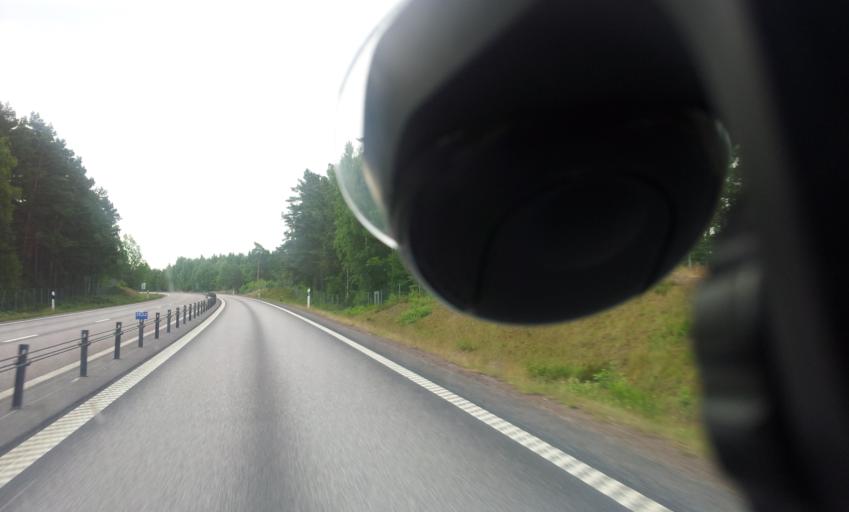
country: SE
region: Kalmar
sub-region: Oskarshamns Kommun
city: Paskallavik
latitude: 57.1612
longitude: 16.4466
